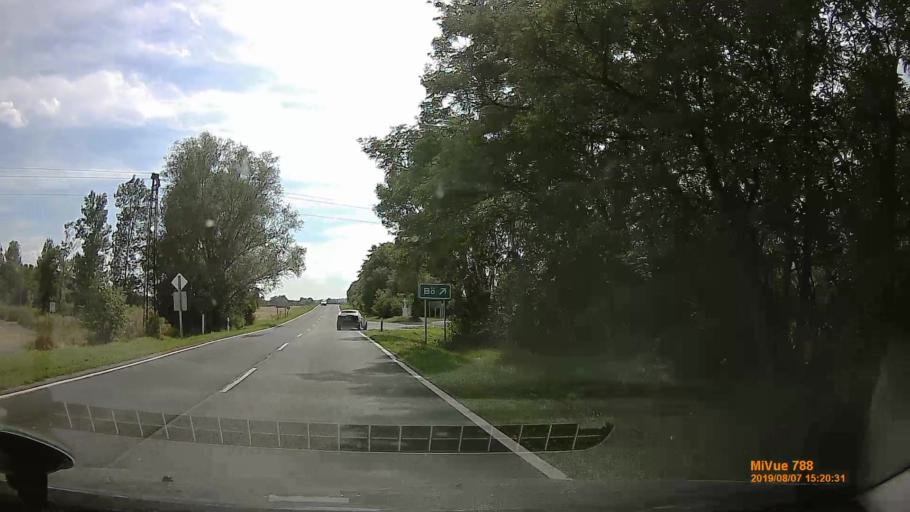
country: HU
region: Vas
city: Sarvar
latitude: 47.3480
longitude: 16.8758
